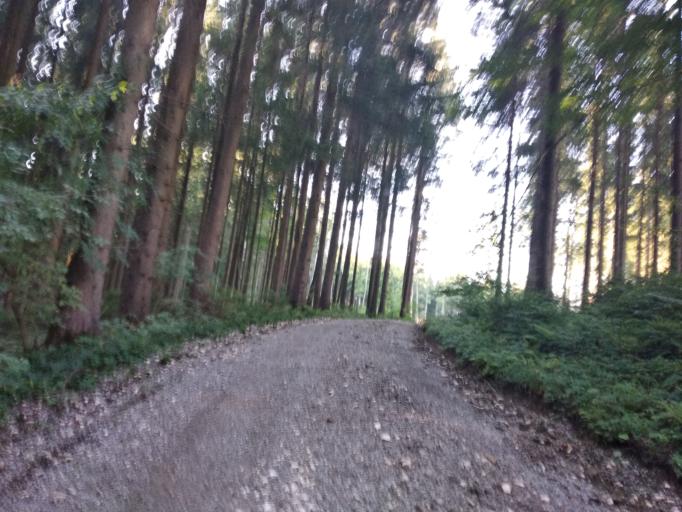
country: DE
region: Bavaria
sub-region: Swabia
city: Lautrach
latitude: 47.8844
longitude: 10.1032
